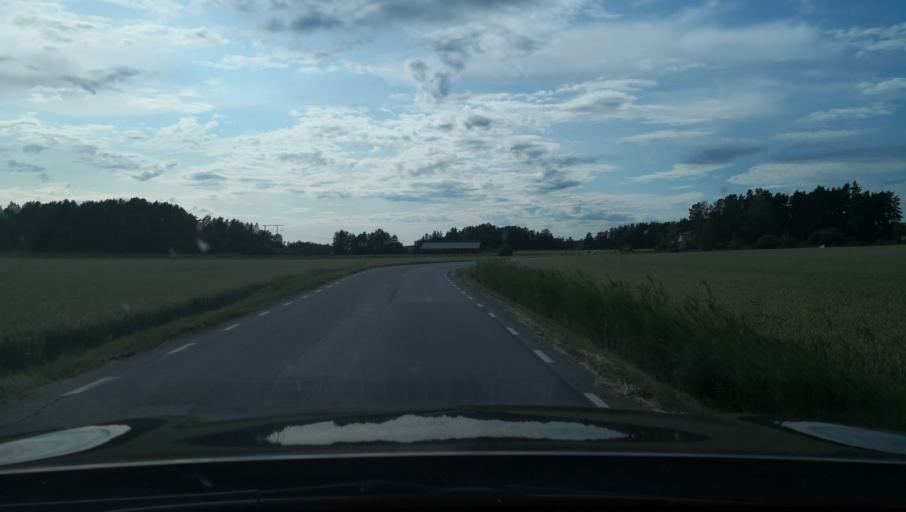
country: SE
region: Uppsala
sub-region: Enkopings Kommun
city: Orsundsbro
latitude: 59.6802
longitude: 17.4092
